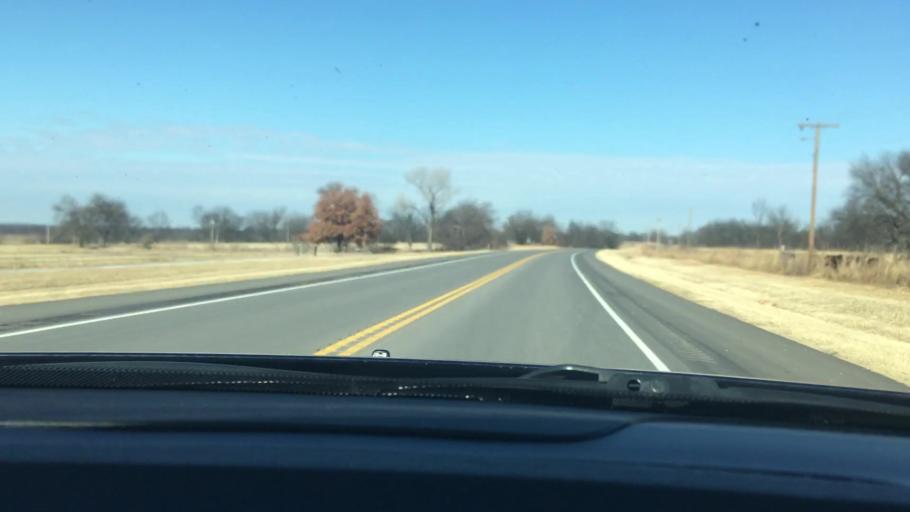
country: US
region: Oklahoma
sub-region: Murray County
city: Davis
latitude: 34.5470
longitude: -97.1314
